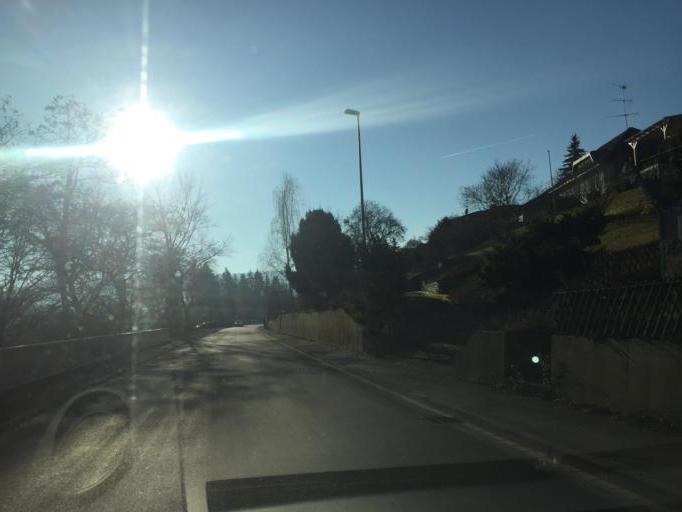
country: DE
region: Baden-Wuerttemberg
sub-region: Freiburg Region
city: Busingen
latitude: 47.6946
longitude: 8.6864
